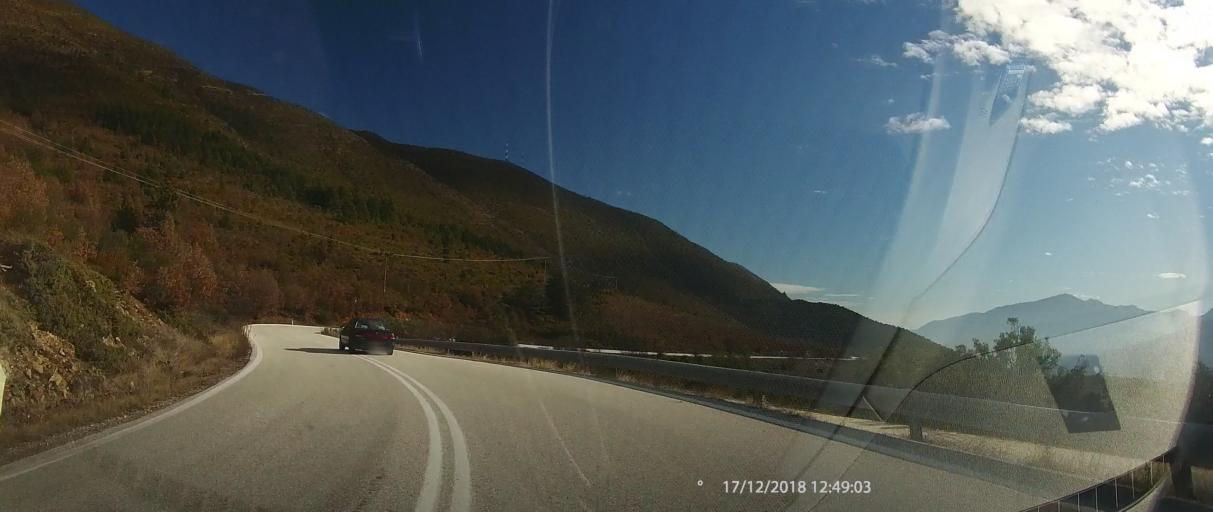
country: GR
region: Thessaly
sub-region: Trikala
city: Kastraki
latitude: 39.7806
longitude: 21.4411
